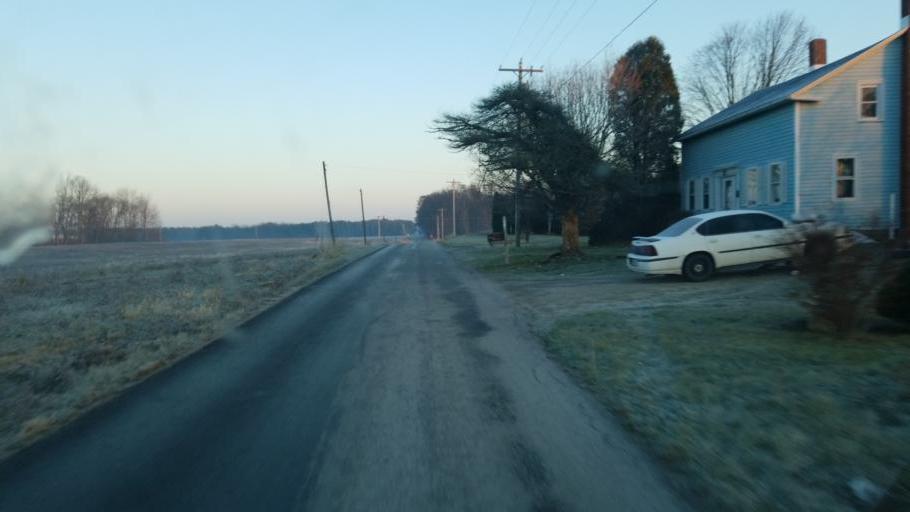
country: US
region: Ohio
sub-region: Wayne County
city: West Salem
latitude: 40.9717
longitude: -82.0780
